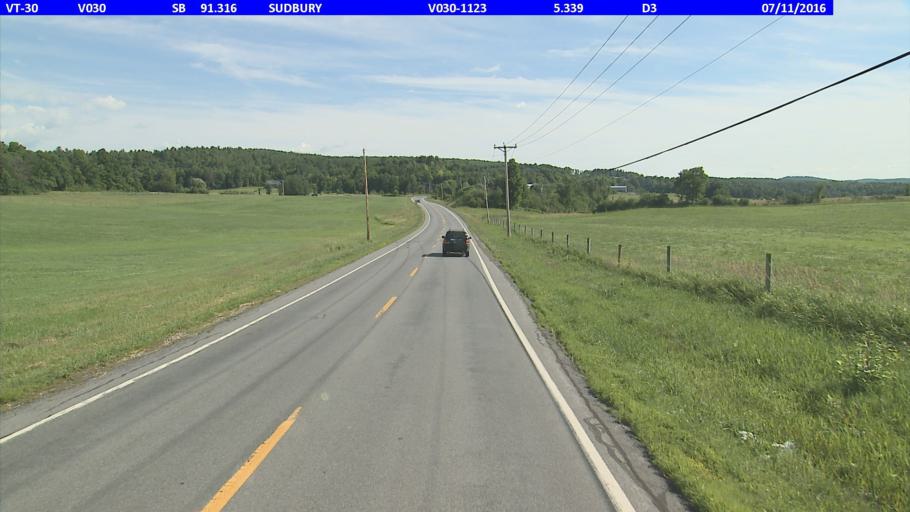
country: US
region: Vermont
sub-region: Rutland County
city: Brandon
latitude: 43.8230
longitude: -73.1936
